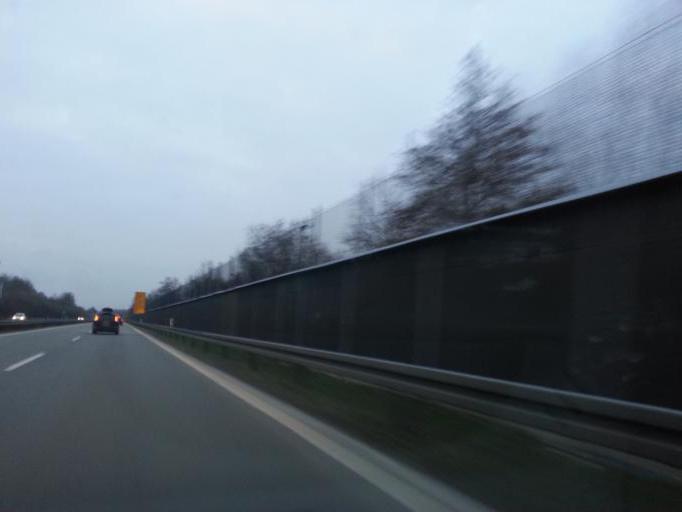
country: DE
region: Baden-Wuerttemberg
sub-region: Tuebingen Region
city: Ravensburg
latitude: 47.7888
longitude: 9.6018
